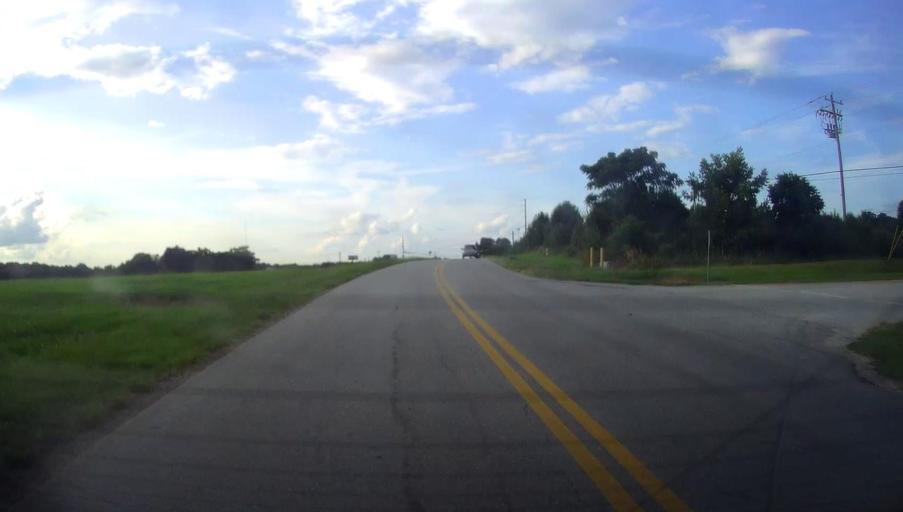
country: US
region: Georgia
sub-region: Monroe County
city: Forsyth
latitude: 33.0250
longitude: -83.9136
